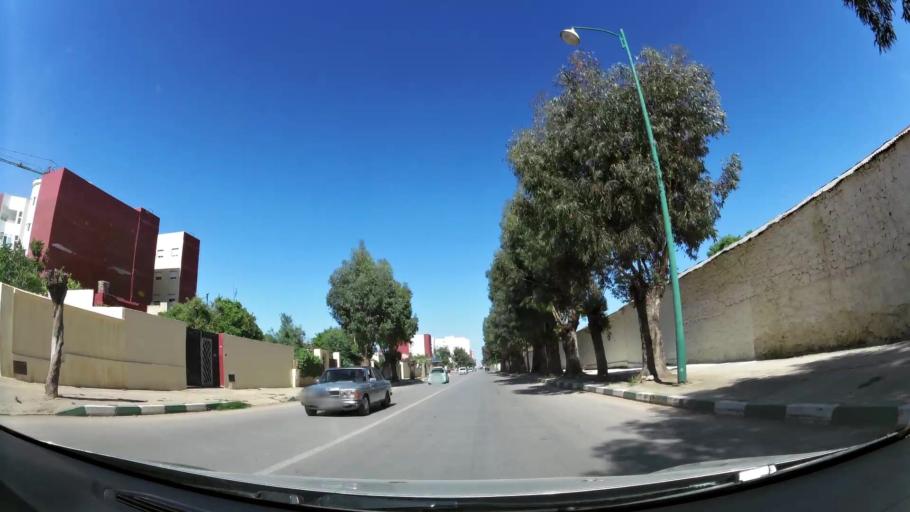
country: MA
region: Meknes-Tafilalet
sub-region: Meknes
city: Meknes
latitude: 33.8923
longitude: -5.5349
